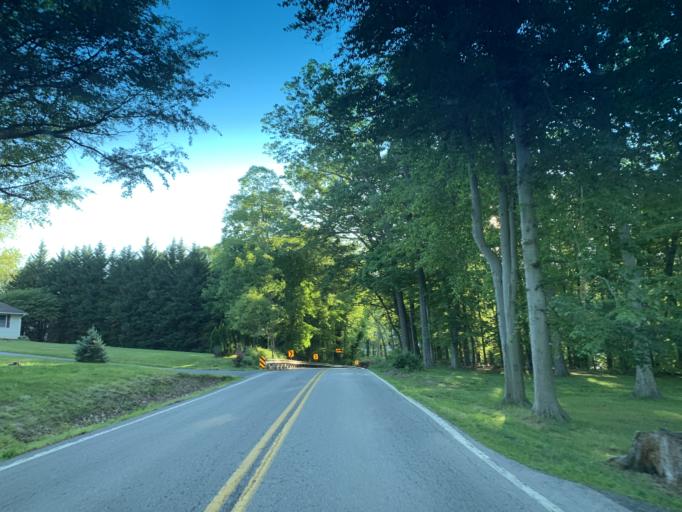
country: US
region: Maryland
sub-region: Cecil County
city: Elkton
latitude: 39.6627
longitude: -75.8350
